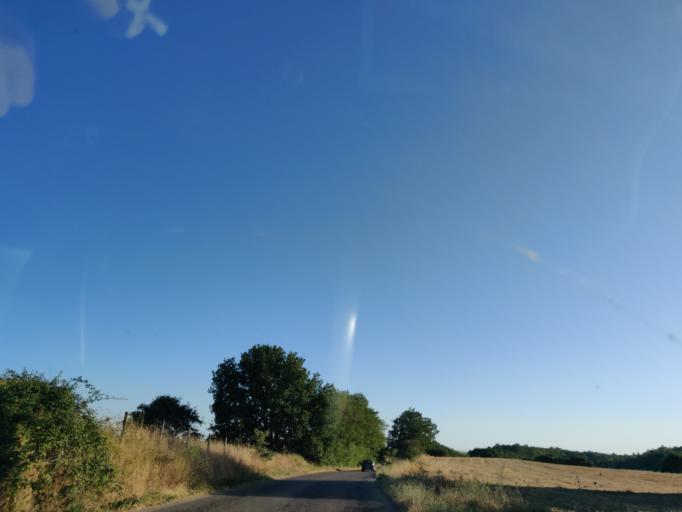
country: IT
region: Latium
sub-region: Provincia di Viterbo
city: Grotte di Castro
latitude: 42.6998
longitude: 11.8799
